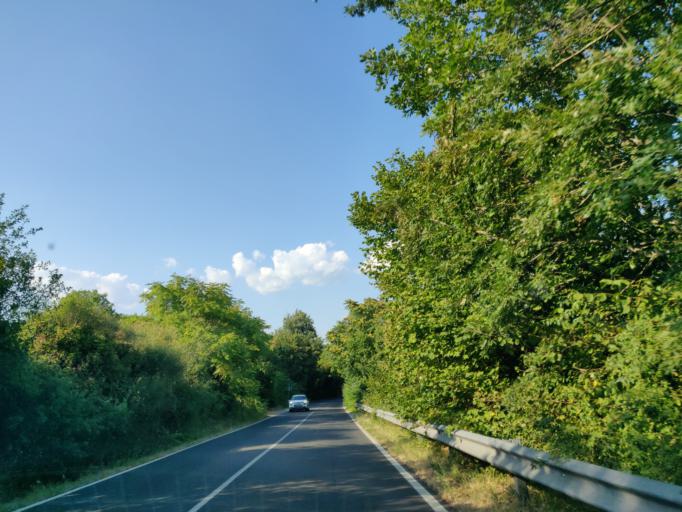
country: IT
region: Latium
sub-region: Provincia di Viterbo
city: Gradoli
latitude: 42.6481
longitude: 11.8410
